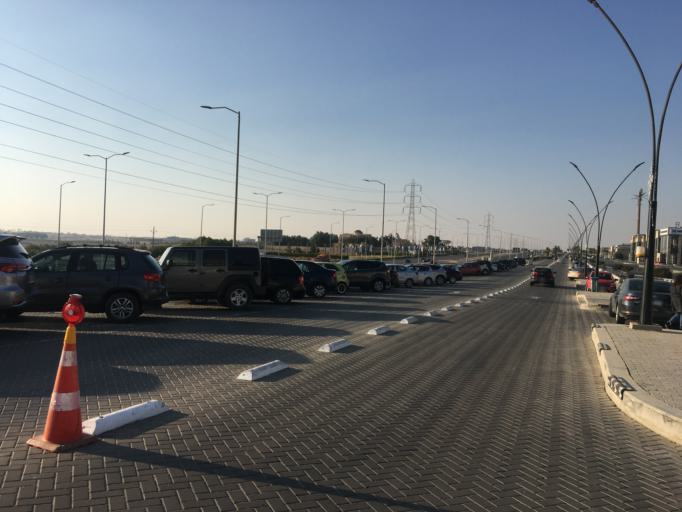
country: EG
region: Al Jizah
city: Awsim
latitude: 30.0555
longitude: 30.9423
